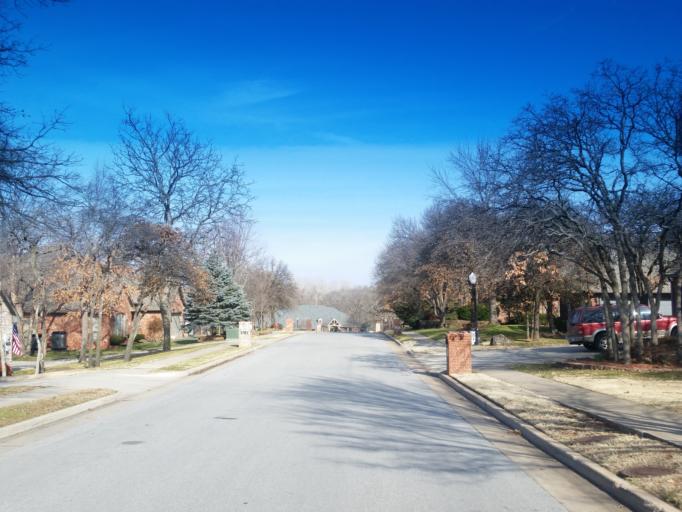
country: US
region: Oklahoma
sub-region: Oklahoma County
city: Edmond
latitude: 35.6462
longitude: -97.4332
